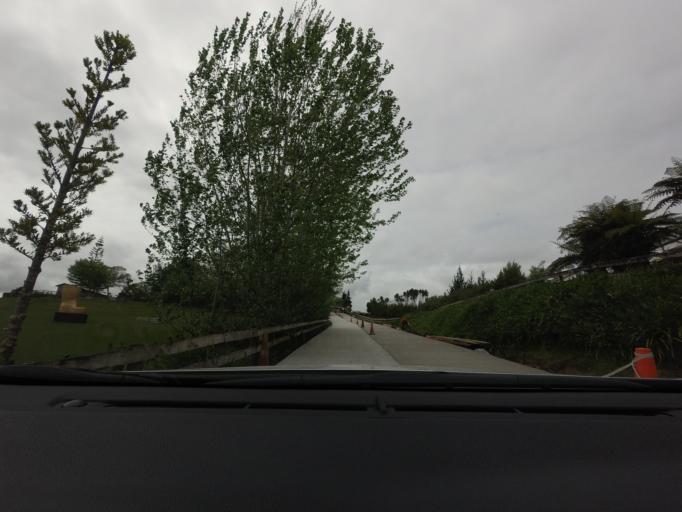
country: NZ
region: Auckland
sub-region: Auckland
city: Waitakere
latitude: -36.8961
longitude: 174.6004
